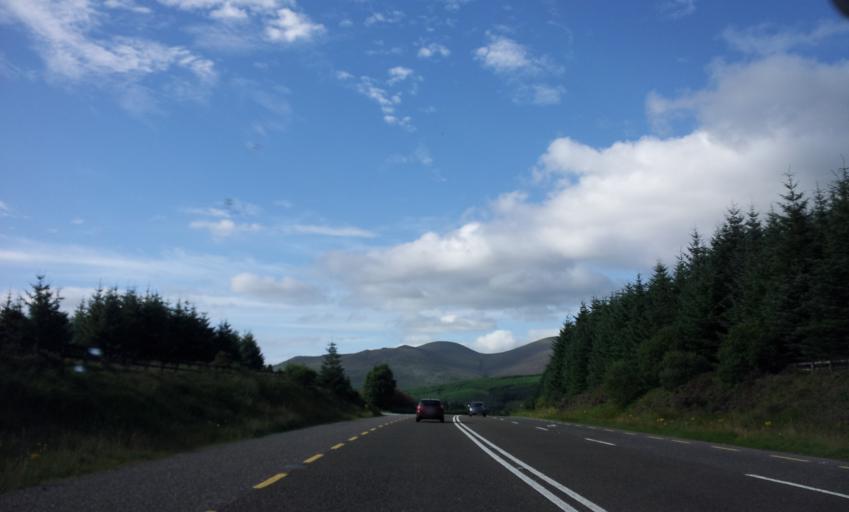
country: IE
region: Munster
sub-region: County Cork
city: Millstreet
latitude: 51.9702
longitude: -9.2519
